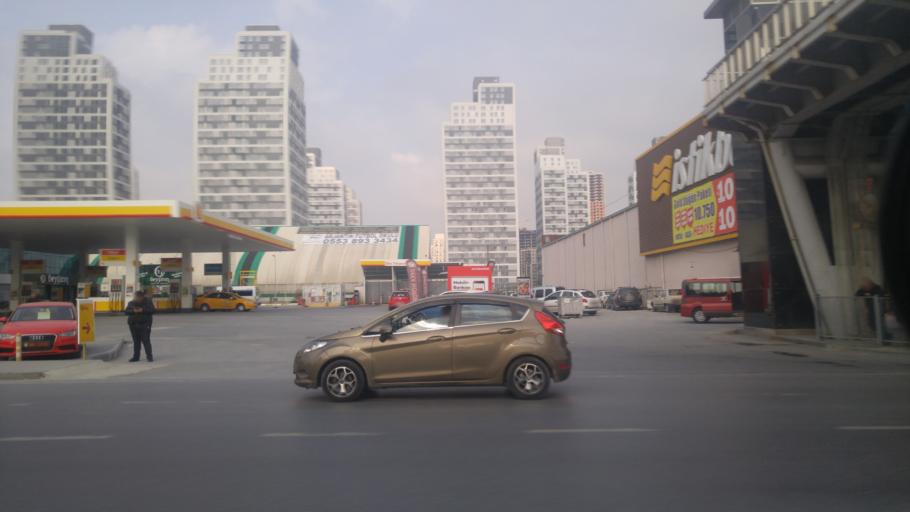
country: TR
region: Istanbul
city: Gurpinar
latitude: 41.0194
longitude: 28.6316
